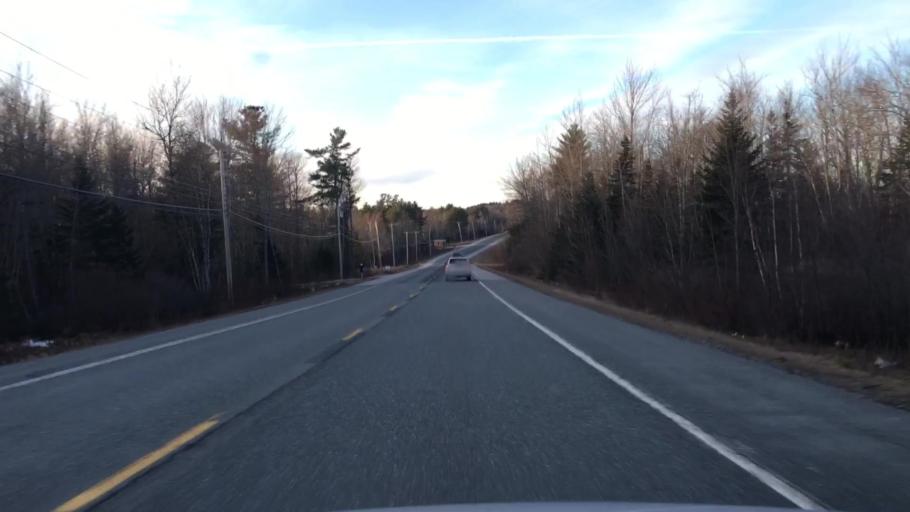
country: US
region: Maine
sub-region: Hancock County
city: Dedham
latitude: 44.6314
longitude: -68.5419
